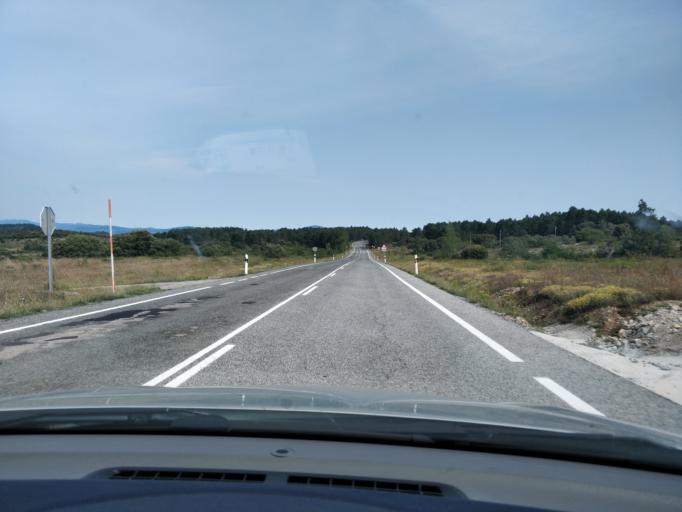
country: ES
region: Cantabria
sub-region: Provincia de Cantabria
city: San Martin de Elines
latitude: 42.9503
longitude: -3.7579
